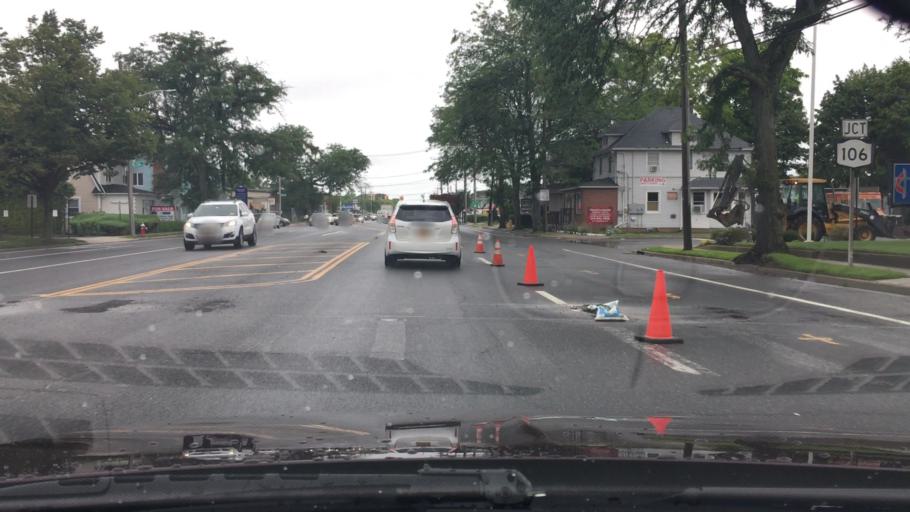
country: US
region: New York
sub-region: Nassau County
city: Hicksville
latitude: 40.7625
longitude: -73.5255
